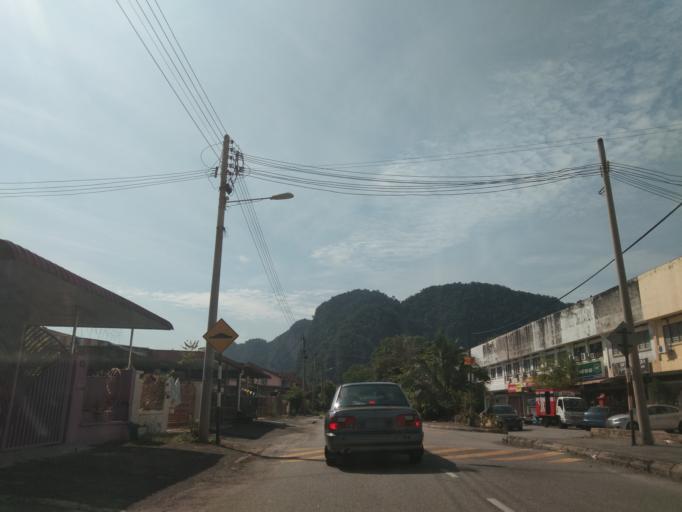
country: MY
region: Perak
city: Ipoh
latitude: 4.5670
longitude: 101.1295
